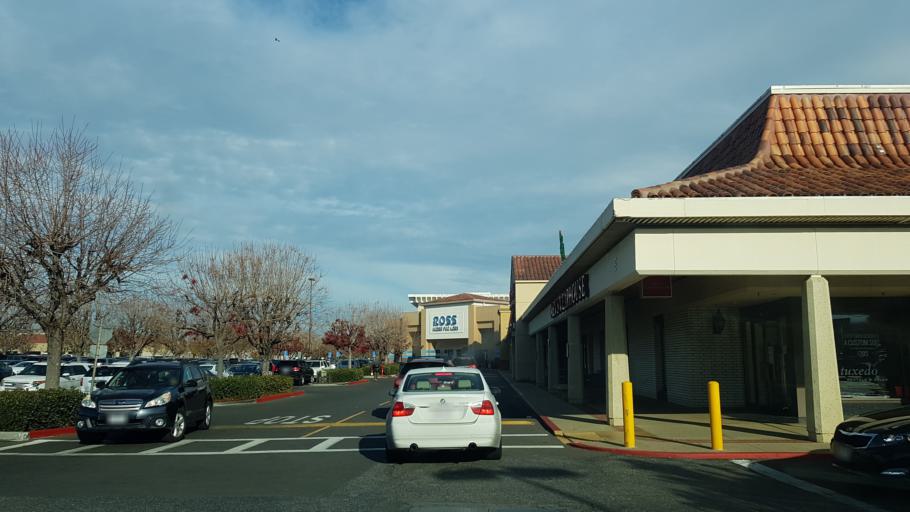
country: US
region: California
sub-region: Santa Clara County
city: Seven Trees
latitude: 37.2511
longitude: -121.8780
